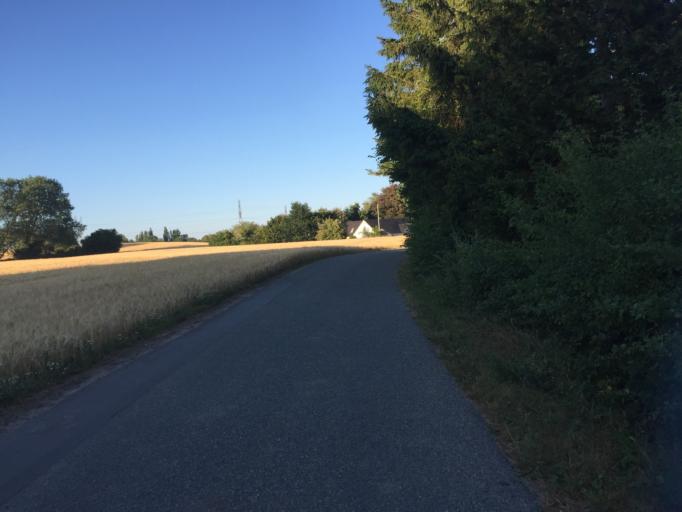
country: DK
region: South Denmark
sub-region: Odense Kommune
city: Bellinge
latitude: 55.3680
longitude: 10.2820
